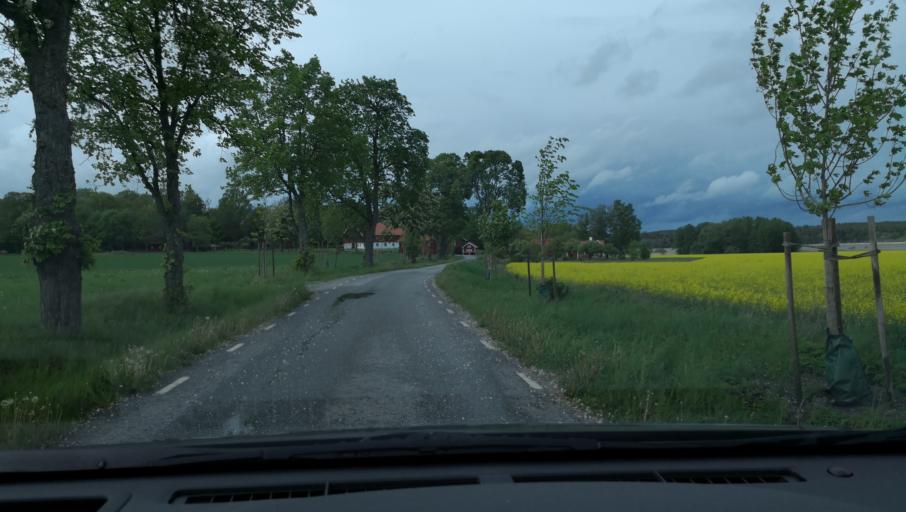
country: SE
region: Uppsala
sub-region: Enkopings Kommun
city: Orsundsbro
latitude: 59.7228
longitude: 17.4189
